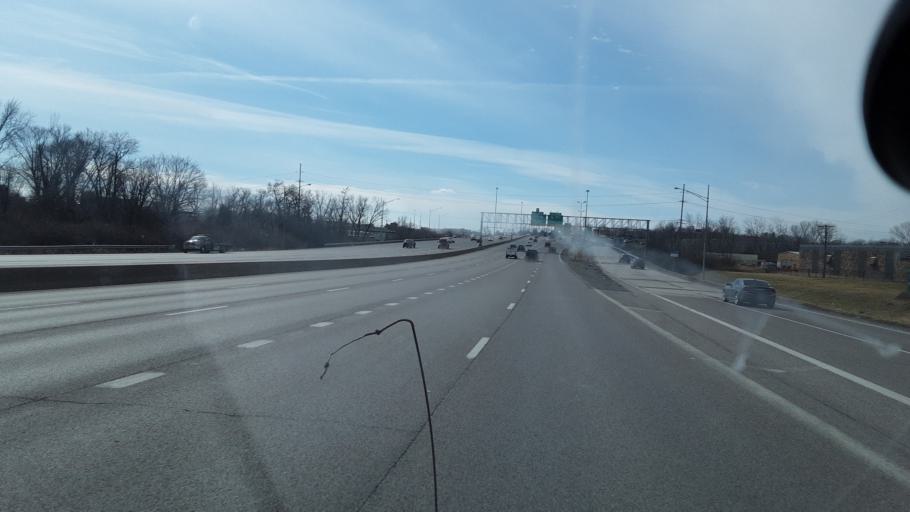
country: US
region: Missouri
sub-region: Saint Louis County
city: Bridgeton
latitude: 38.7614
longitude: -90.4287
